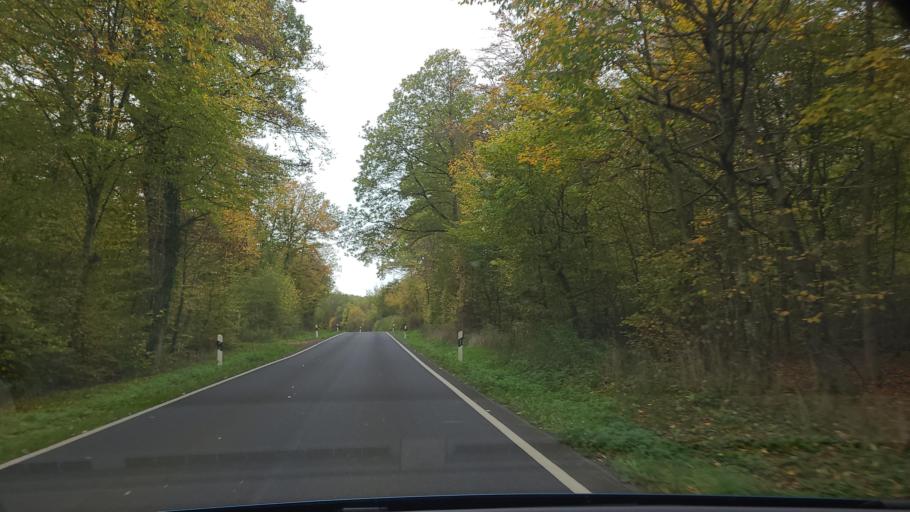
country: LU
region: Luxembourg
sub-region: Canton de Capellen
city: Mamer
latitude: 49.6115
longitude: 6.0096
